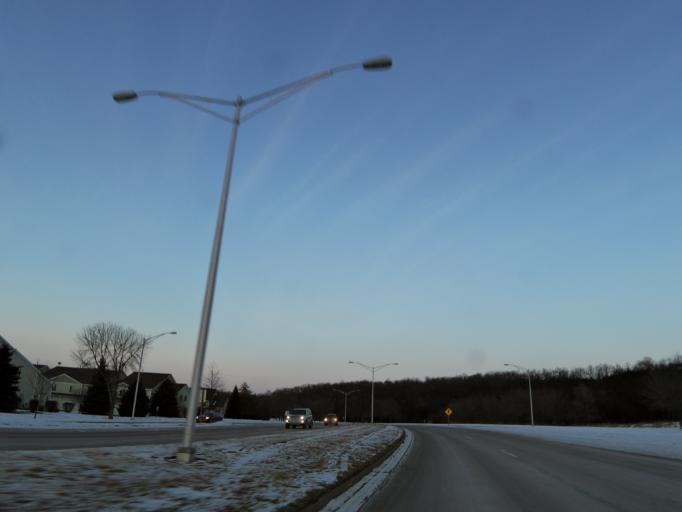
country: US
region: Wisconsin
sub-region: Saint Croix County
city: Hudson
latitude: 44.9486
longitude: -92.7243
